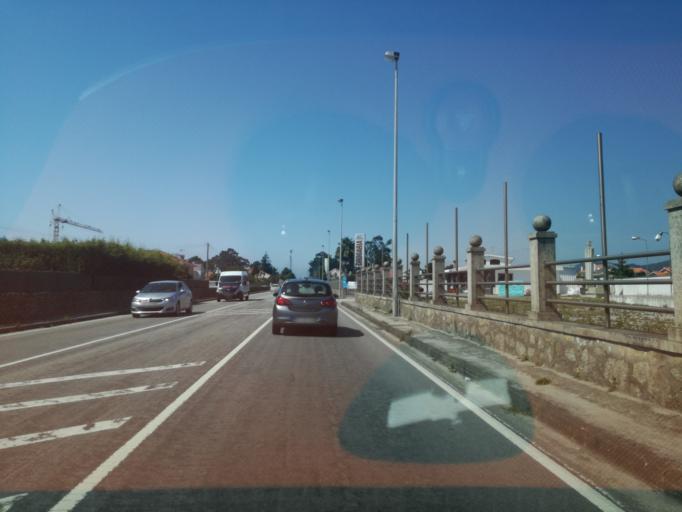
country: PT
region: Braga
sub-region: Esposende
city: Esposende
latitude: 41.5335
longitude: -8.7772
